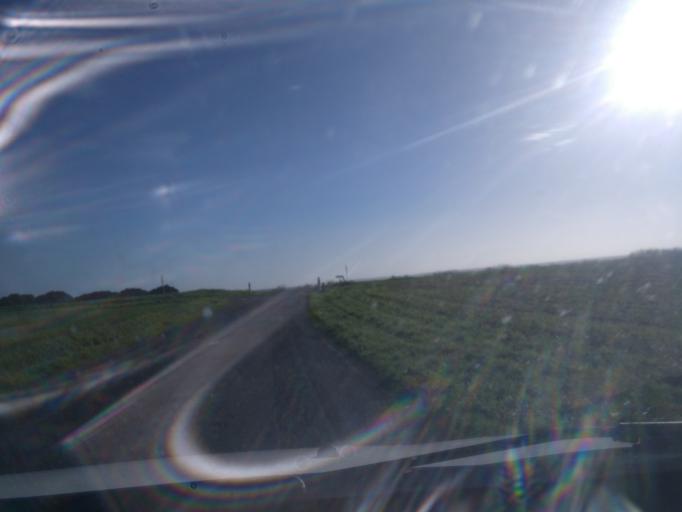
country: FR
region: Brittany
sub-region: Departement d'Ille-et-Vilaine
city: Pleine-Fougeres
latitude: 48.5337
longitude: -1.5437
